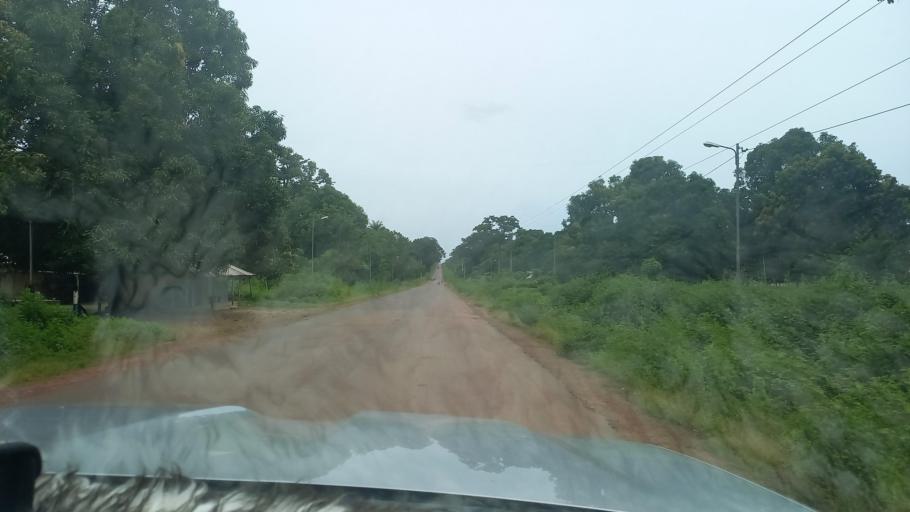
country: SN
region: Ziguinchor
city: Bignona
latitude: 12.8225
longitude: -16.1767
